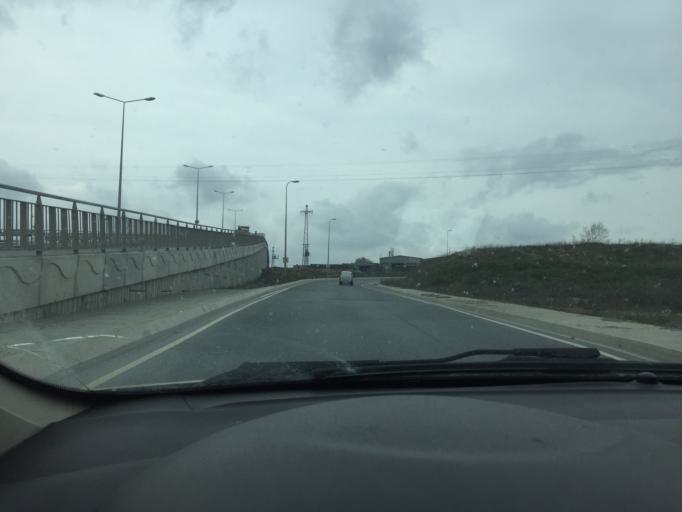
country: TR
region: Istanbul
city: Basaksehir
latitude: 41.1423
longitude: 28.7966
